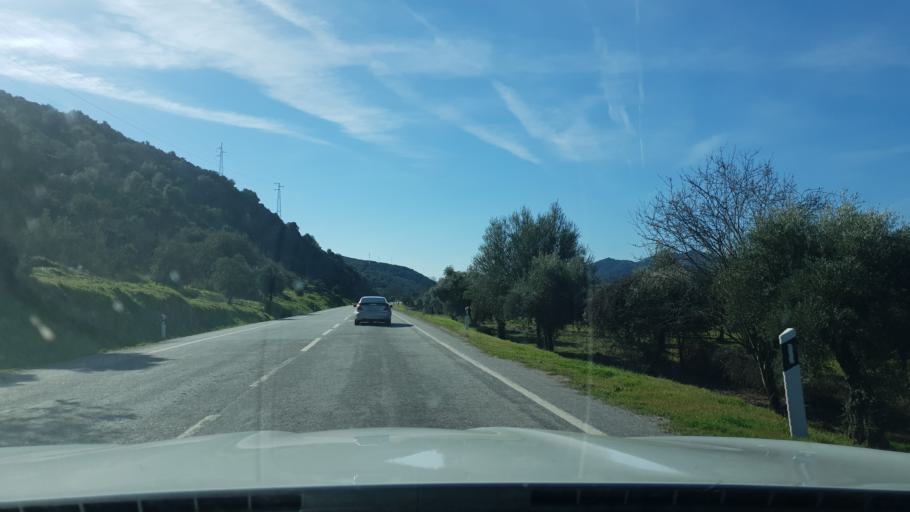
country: PT
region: Braganca
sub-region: Torre de Moncorvo
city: Torre de Moncorvo
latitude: 41.1884
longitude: -7.1001
